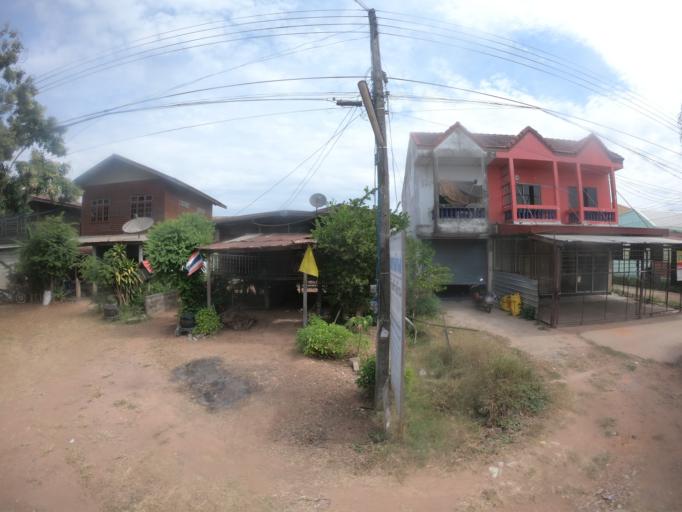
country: TH
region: Maha Sarakham
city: Chiang Yuen
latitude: 16.3935
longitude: 103.1004
